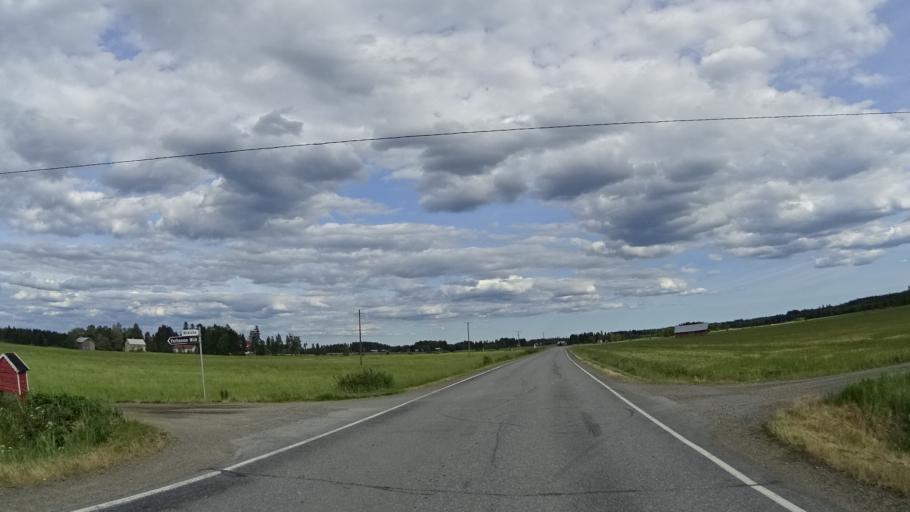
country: FI
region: Haeme
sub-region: Forssa
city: Forssa
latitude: 60.9360
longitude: 23.5699
